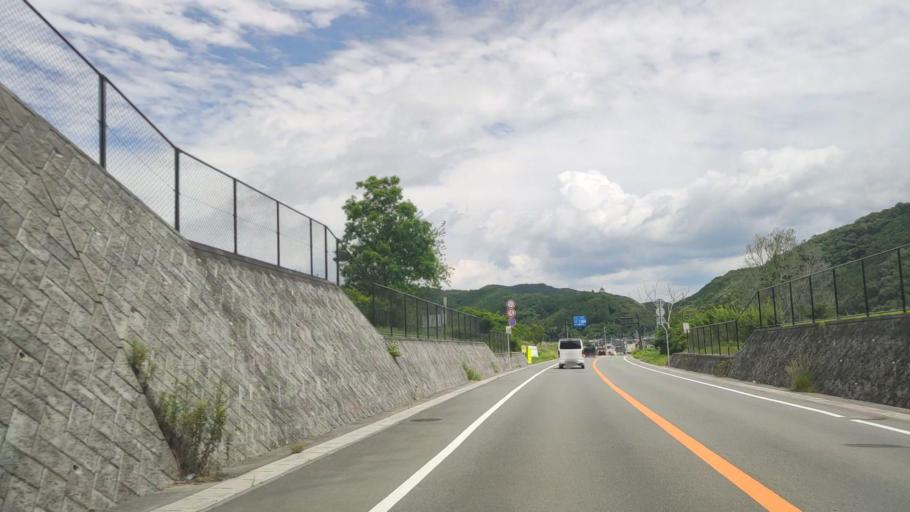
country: JP
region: Hyogo
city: Yamazakicho-nakabirose
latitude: 34.9947
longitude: 134.3917
